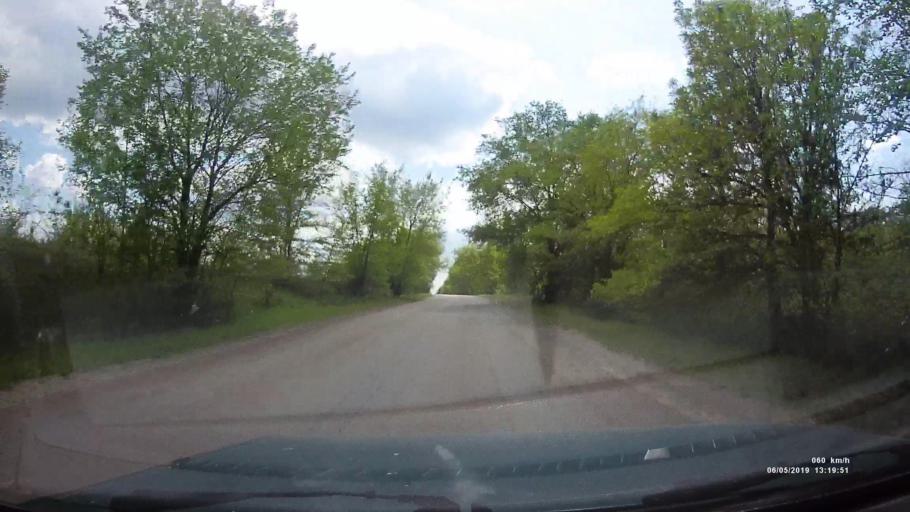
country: RU
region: Rostov
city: Ust'-Donetskiy
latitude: 47.7218
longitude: 40.9125
